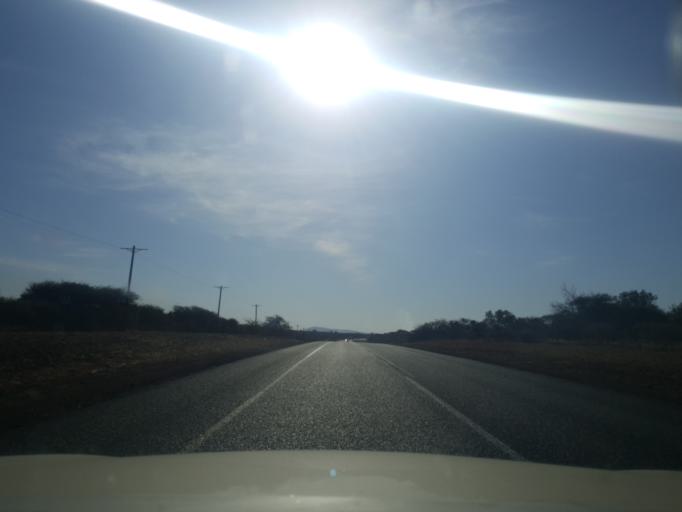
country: ZA
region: North-West
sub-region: Ngaka Modiri Molema District Municipality
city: Zeerust
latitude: -25.5205
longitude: 26.0056
